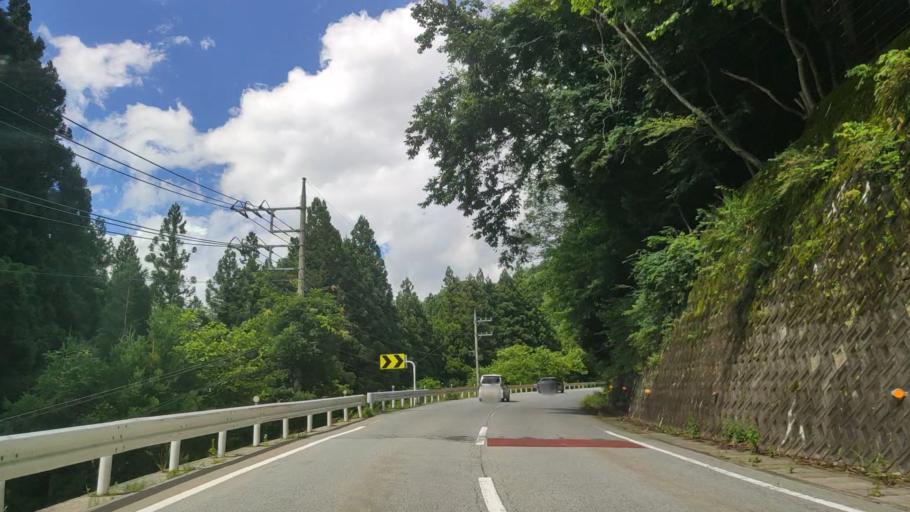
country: JP
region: Yamanashi
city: Enzan
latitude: 35.8268
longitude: 138.7637
